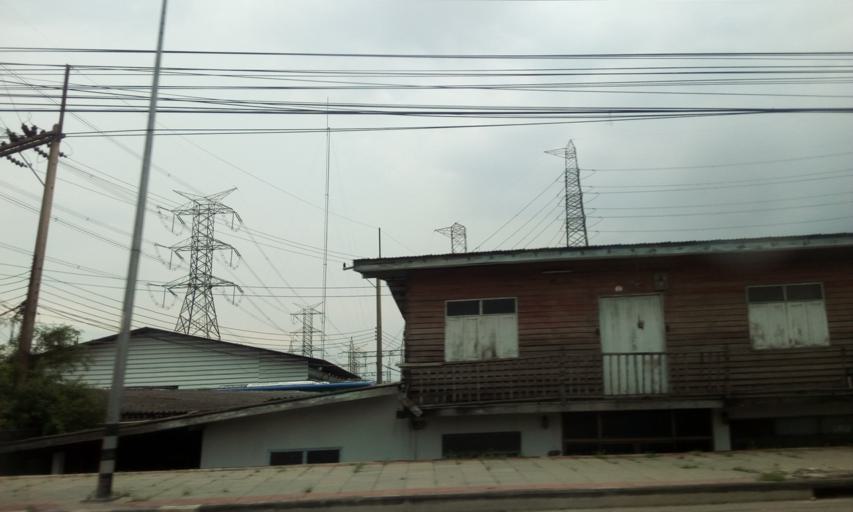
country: TH
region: Phra Nakhon Si Ayutthaya
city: Ban Bang Kadi Pathum Thani
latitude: 13.9725
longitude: 100.5677
